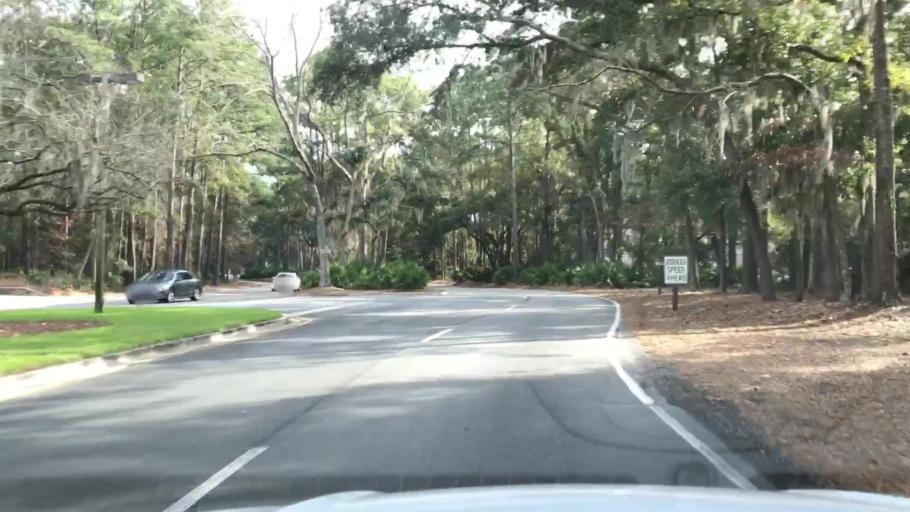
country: US
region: South Carolina
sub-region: Beaufort County
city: Hilton Head Island
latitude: 32.2177
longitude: -80.7232
